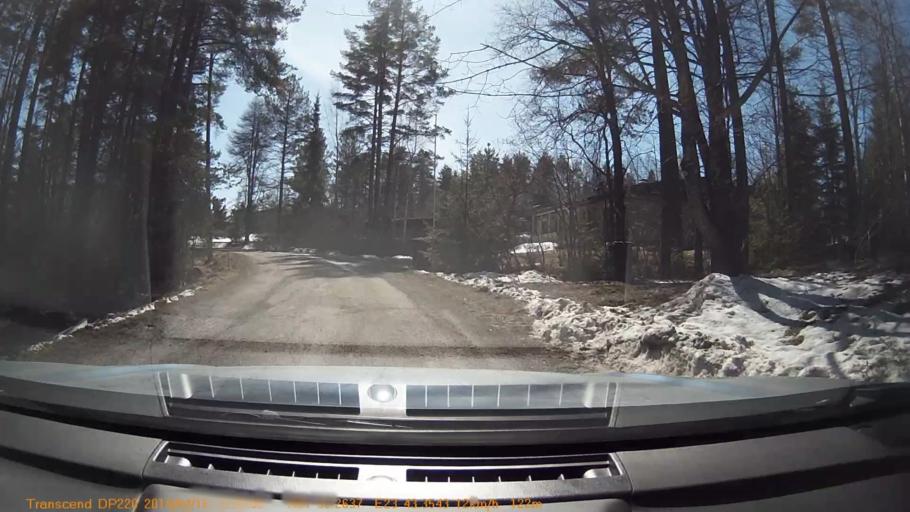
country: FI
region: Pirkanmaa
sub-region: Tampere
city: Kuru
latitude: 61.8711
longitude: 23.7225
